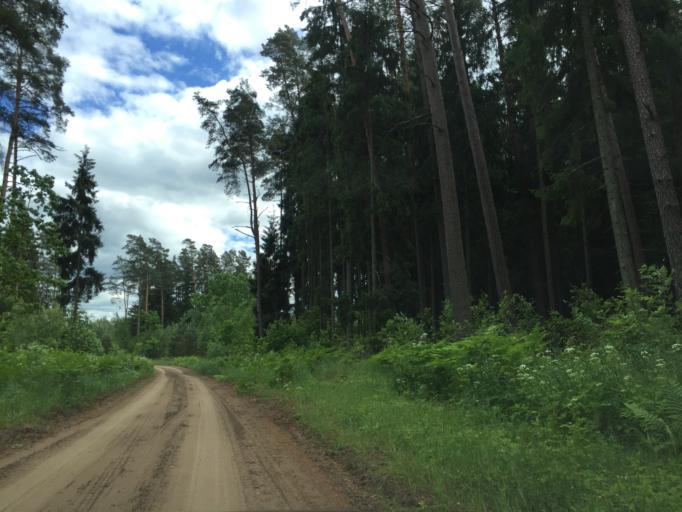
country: LV
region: Lecava
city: Iecava
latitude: 56.5673
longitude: 24.3014
